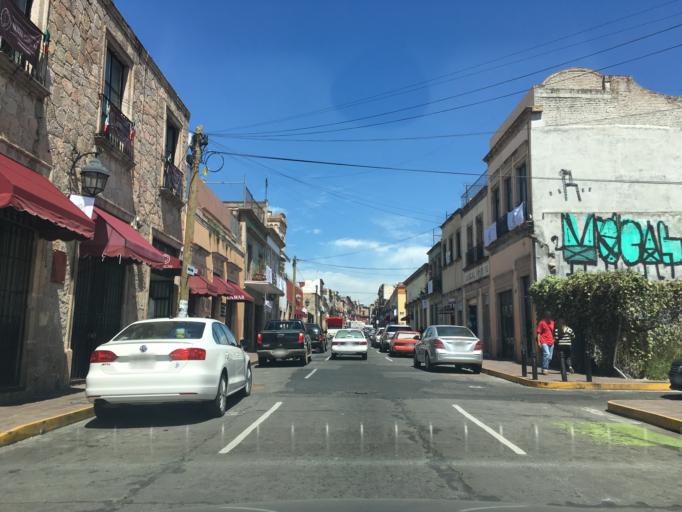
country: MX
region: Michoacan
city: Morelia
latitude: 19.6981
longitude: -101.1942
